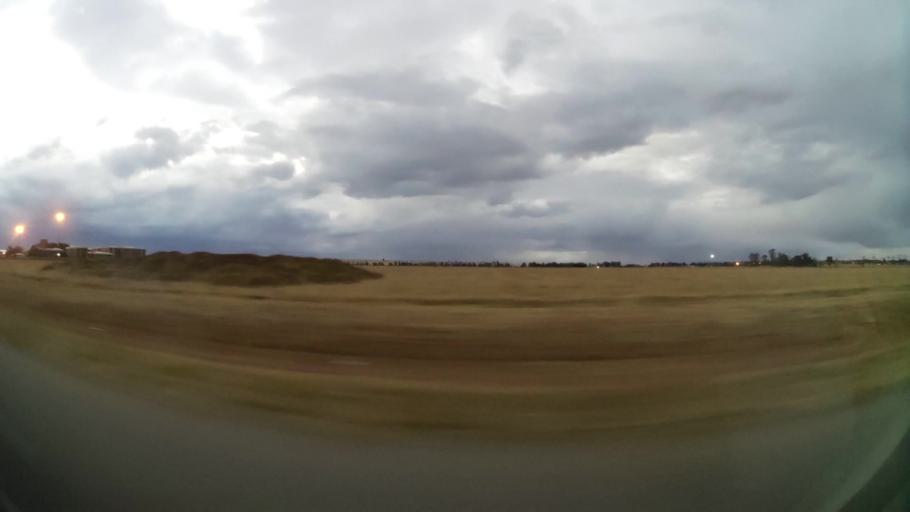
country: ZA
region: Orange Free State
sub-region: Lejweleputswa District Municipality
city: Welkom
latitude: -27.9508
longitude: 26.7934
